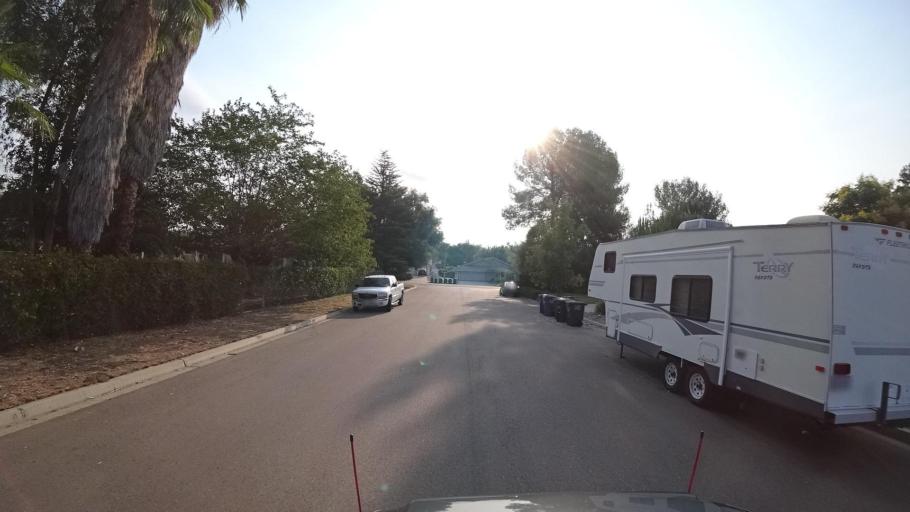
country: US
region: California
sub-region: San Diego County
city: San Diego Country Estates
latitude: 33.0133
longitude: -116.8182
